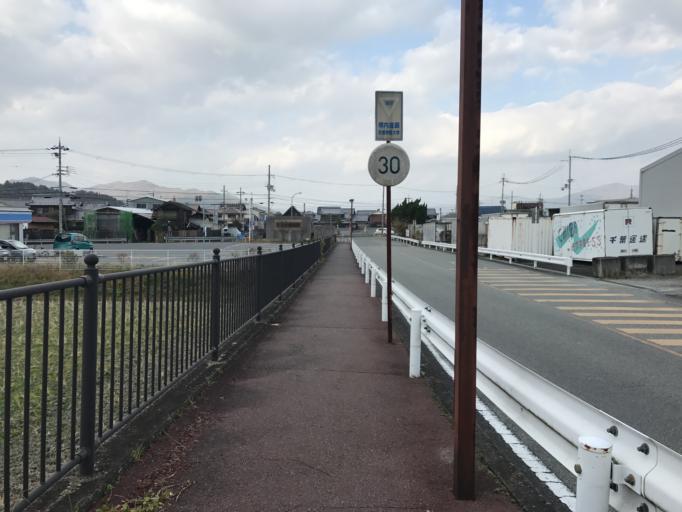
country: JP
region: Kyoto
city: Kameoka
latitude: 34.9972
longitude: 135.5516
